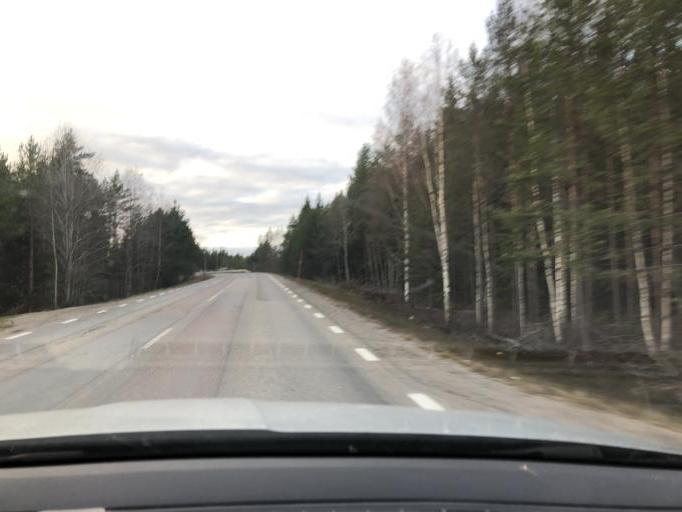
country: SE
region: Gaevleborg
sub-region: Hudiksvalls Kommun
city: Iggesund
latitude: 61.5521
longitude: 16.9816
